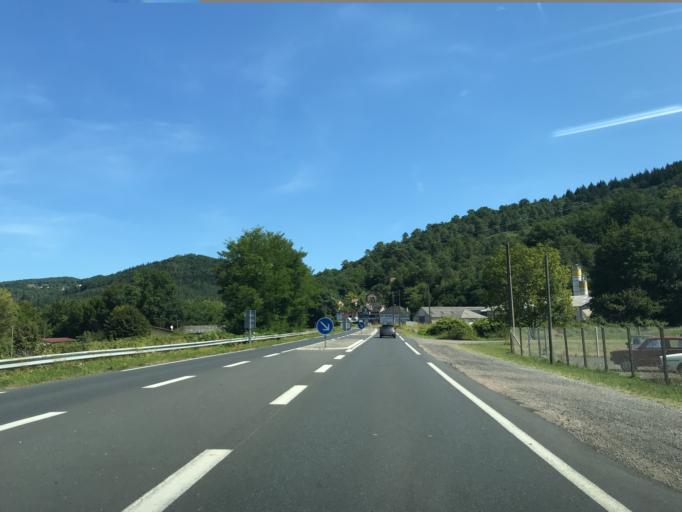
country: FR
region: Limousin
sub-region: Departement de la Correze
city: Cornil
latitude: 45.1959
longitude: 1.6575
